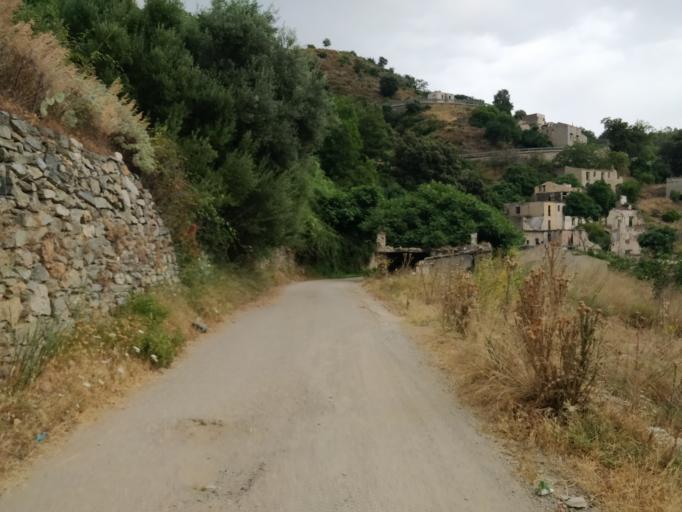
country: IT
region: Sardinia
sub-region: Provincia di Ogliastra
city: Gairo Sant'Elena
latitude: 39.8487
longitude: 9.4988
